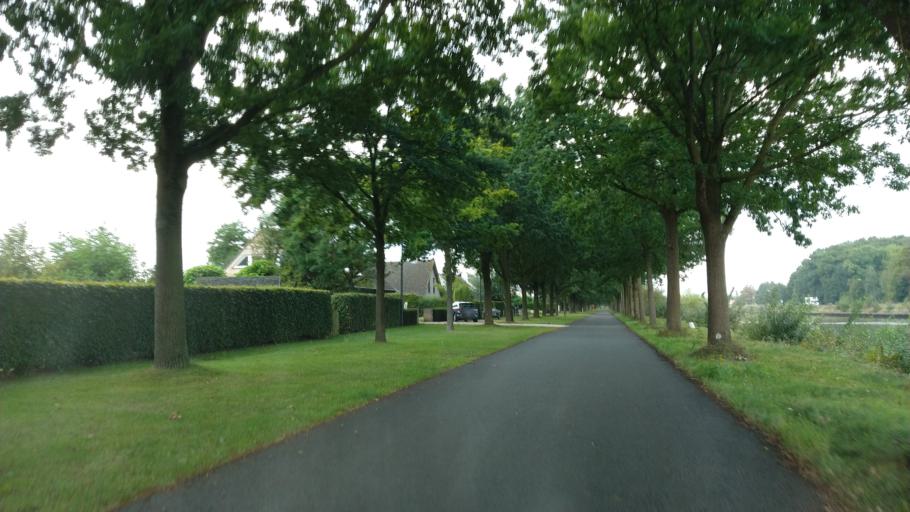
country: BE
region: Flanders
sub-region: Provincie Oost-Vlaanderen
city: Lovendegem
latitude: 51.0910
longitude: 3.6152
